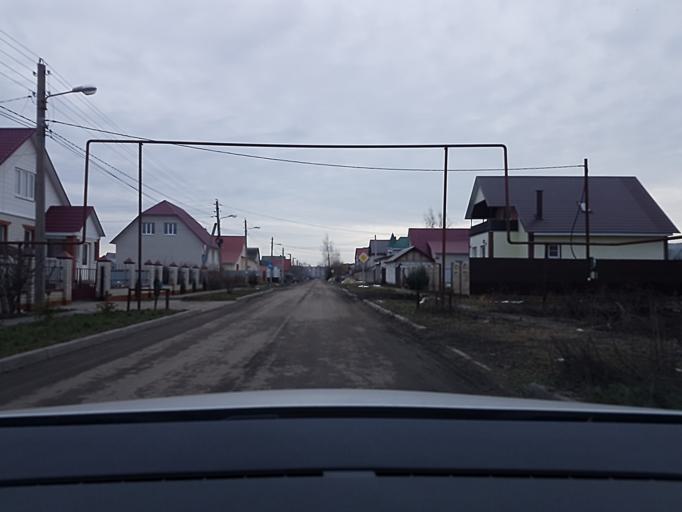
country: RU
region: Tambov
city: Tambov
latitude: 52.7806
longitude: 41.3792
